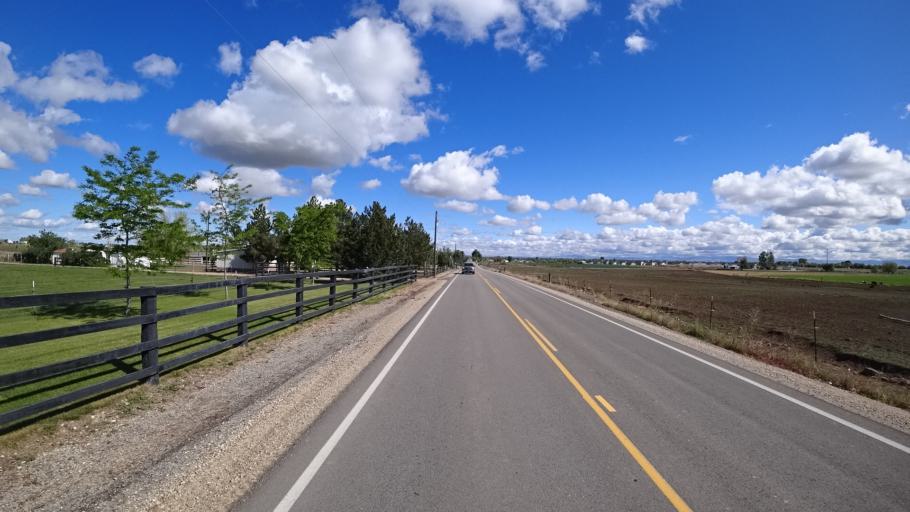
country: US
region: Idaho
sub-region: Ada County
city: Kuna
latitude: 43.4962
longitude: -116.4537
